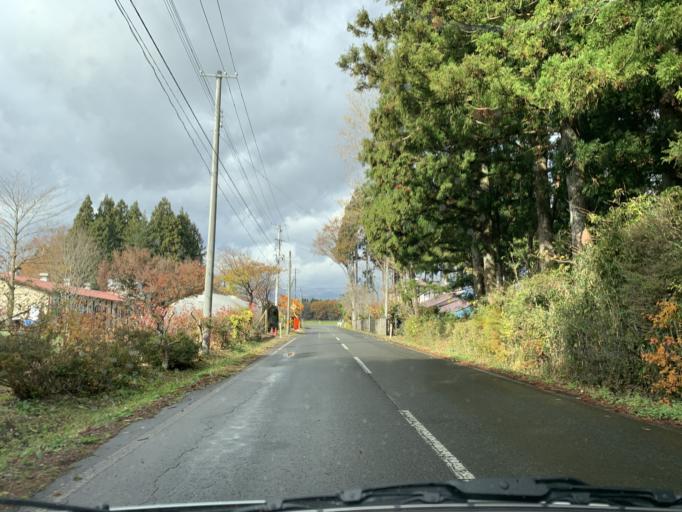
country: JP
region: Iwate
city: Mizusawa
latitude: 39.0897
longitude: 141.0179
